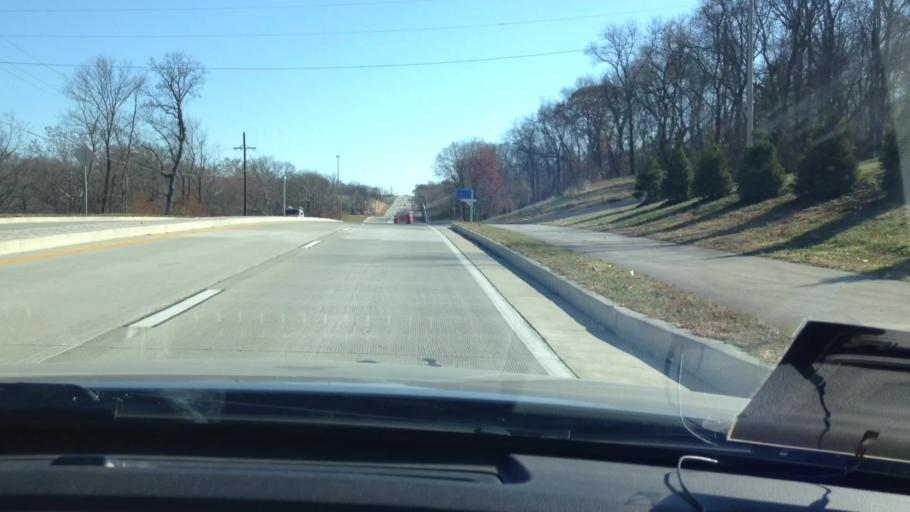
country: US
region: Missouri
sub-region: Platte County
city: Weatherby Lake
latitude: 39.2247
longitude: -94.7501
